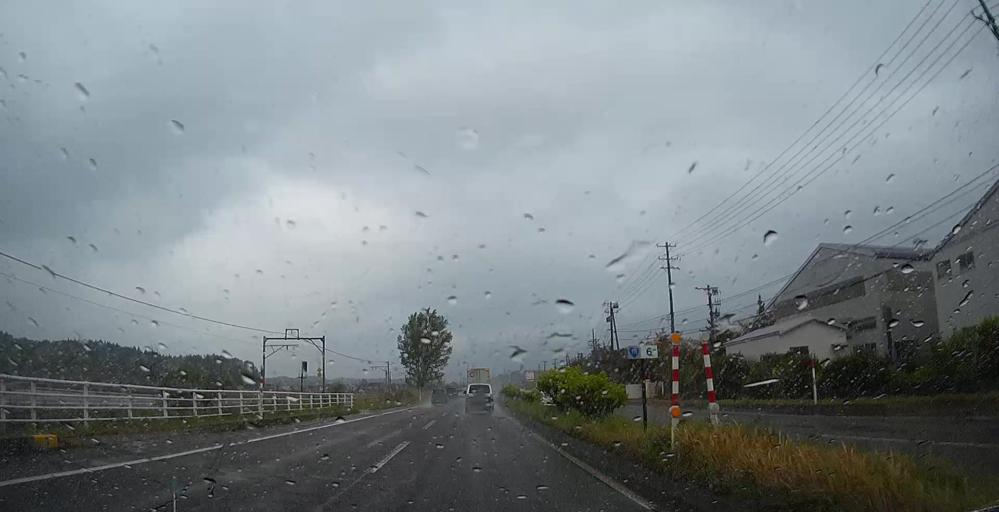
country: JP
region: Niigata
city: Kashiwazaki
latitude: 37.4448
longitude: 138.6351
